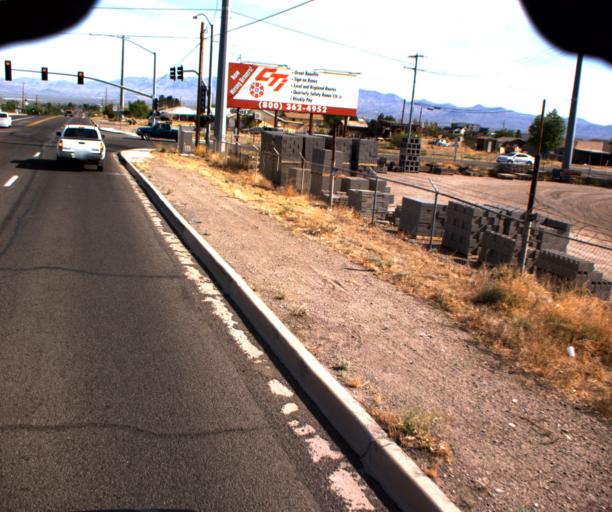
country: US
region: Arizona
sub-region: Graham County
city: Safford
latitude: 32.8019
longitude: -109.7076
